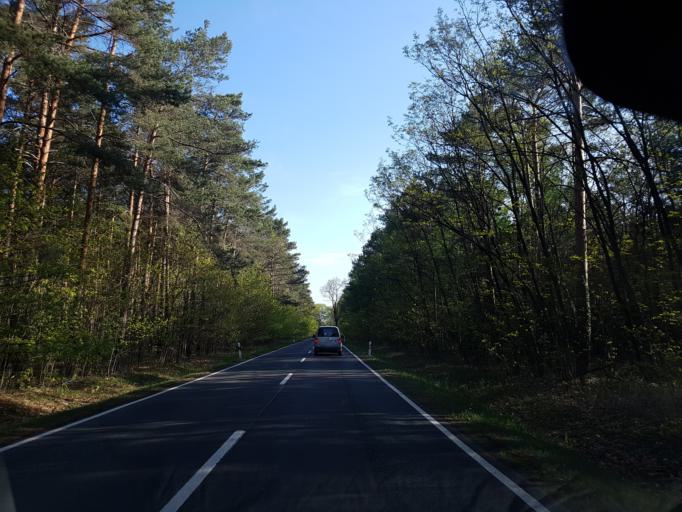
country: DE
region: Brandenburg
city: Grossraschen
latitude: 51.6069
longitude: 14.0190
